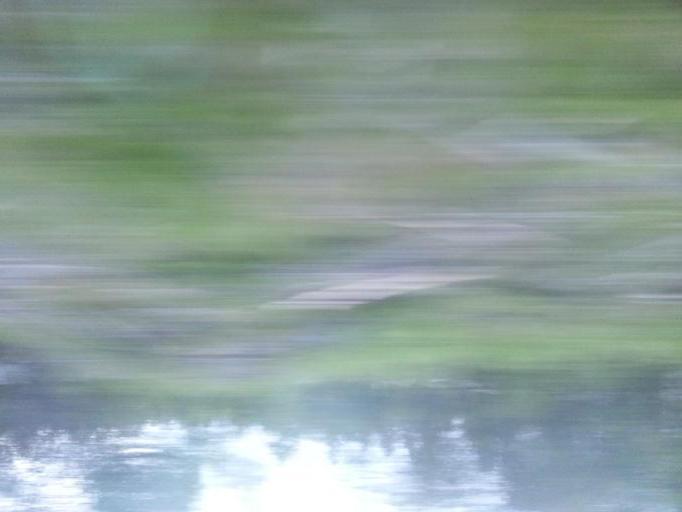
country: NO
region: Oppland
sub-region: Dovre
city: Dombas
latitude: 62.1103
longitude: 9.1011
